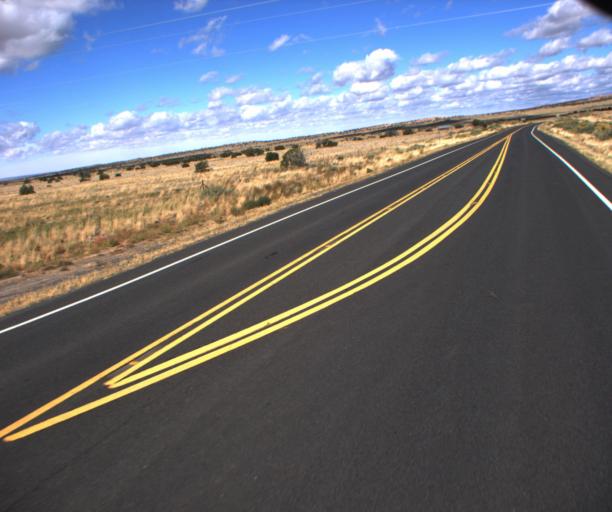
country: US
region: Arizona
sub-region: Apache County
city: Houck
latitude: 35.0469
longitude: -109.2723
